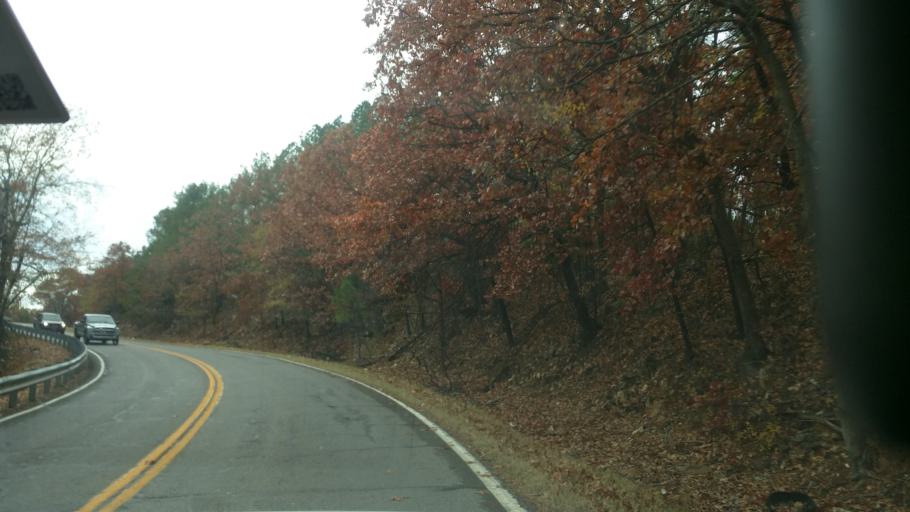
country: US
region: Oklahoma
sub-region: Cherokee County
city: Tahlequah
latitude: 35.9238
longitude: -94.8449
